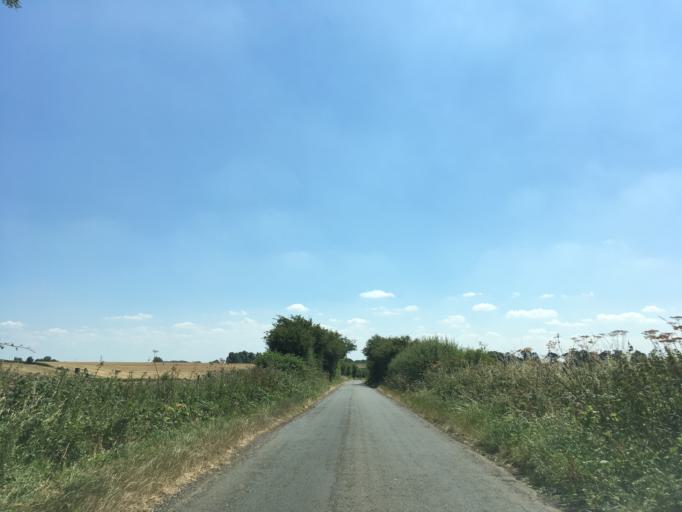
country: GB
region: England
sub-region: Gloucestershire
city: Chalford
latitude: 51.7077
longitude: -2.1115
